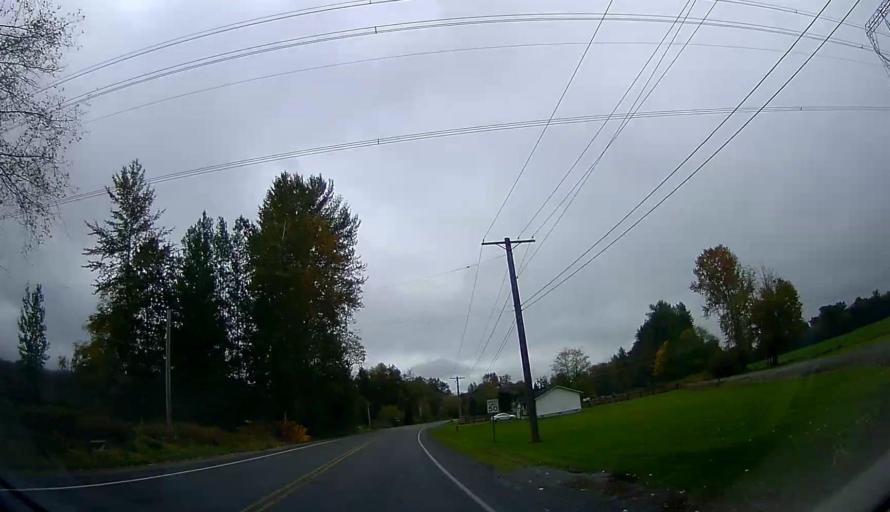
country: US
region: Washington
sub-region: Skagit County
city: Sedro-Woolley
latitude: 48.5233
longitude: -122.1715
